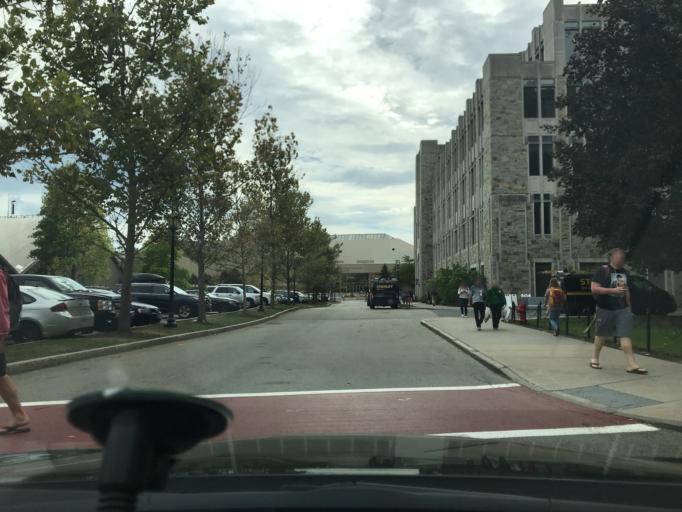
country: US
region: Massachusetts
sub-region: Middlesex County
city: Watertown
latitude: 42.3372
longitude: -71.1685
